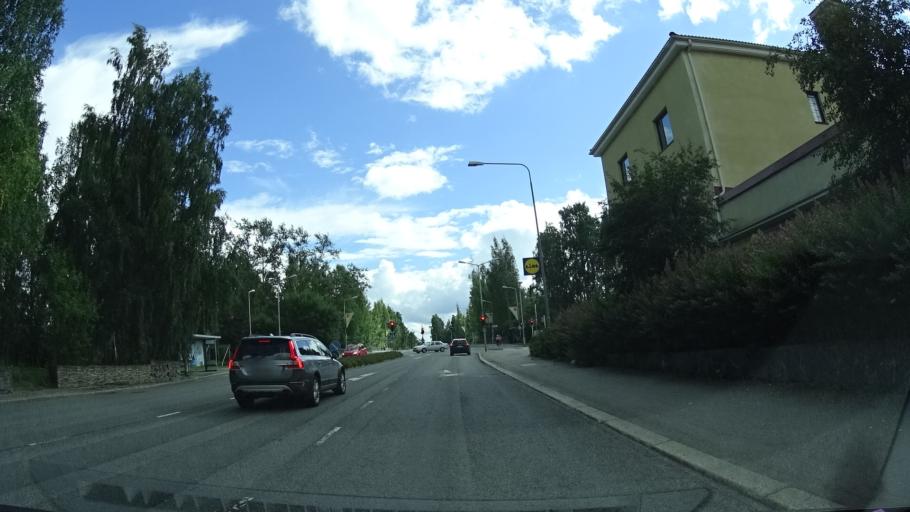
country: FI
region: Pirkanmaa
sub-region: Etelae-Pirkanmaa
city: Valkeakoski
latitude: 61.2767
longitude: 24.0175
